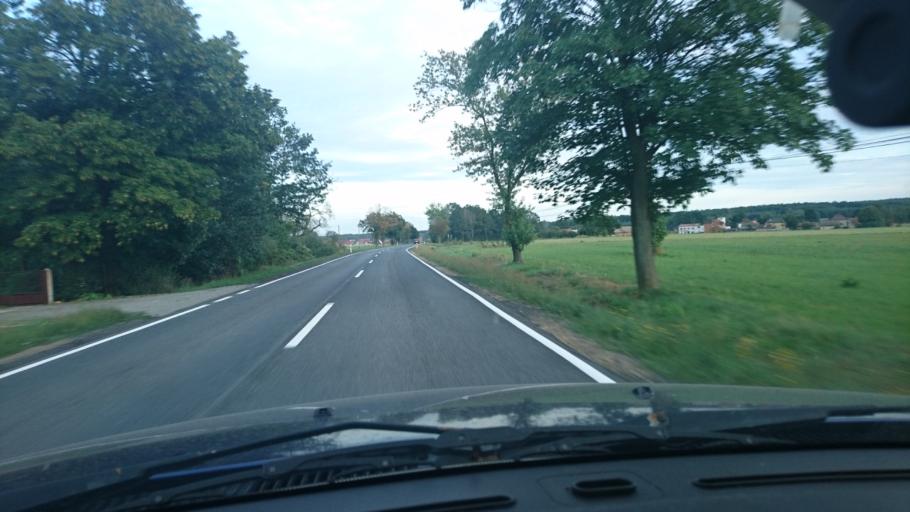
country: PL
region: Silesian Voivodeship
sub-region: Powiat lubliniecki
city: Sierakow Slaski
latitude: 50.8299
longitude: 18.5229
